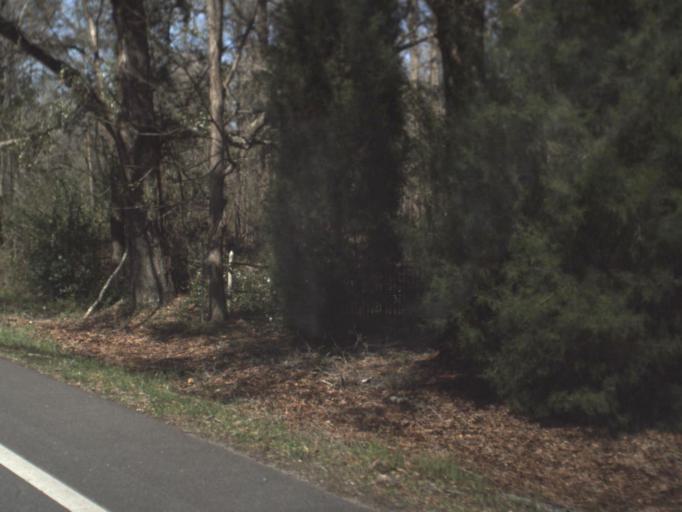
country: US
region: Florida
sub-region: Gadsden County
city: Gretna
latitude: 30.6586
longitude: -84.6920
